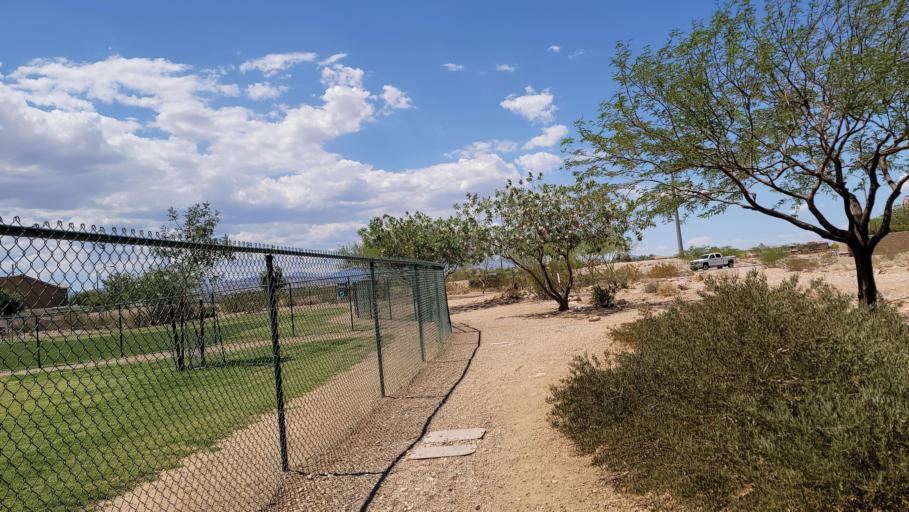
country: US
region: Nevada
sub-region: Clark County
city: Enterprise
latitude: 36.0071
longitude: -115.2856
